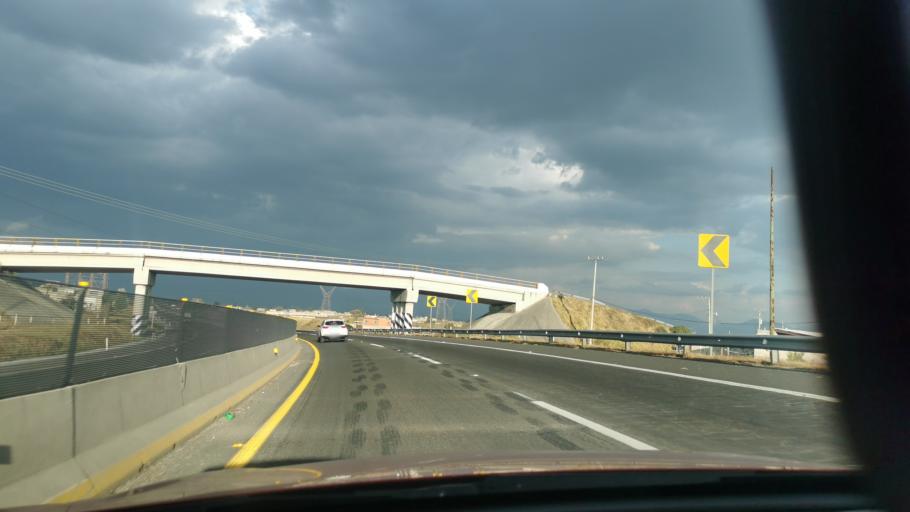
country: MX
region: Mexico
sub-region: Toluca
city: Fraccionamiento Real de San Pablo
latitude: 19.3949
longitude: -99.6380
